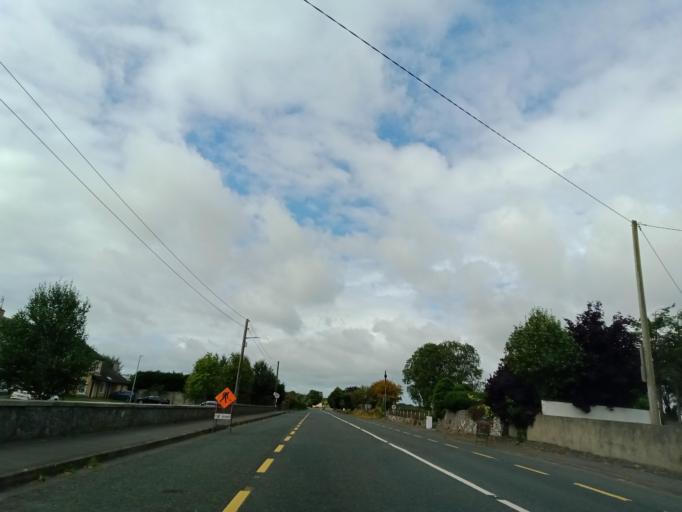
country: IE
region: Leinster
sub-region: Laois
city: Abbeyleix
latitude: 52.8417
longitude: -7.4038
